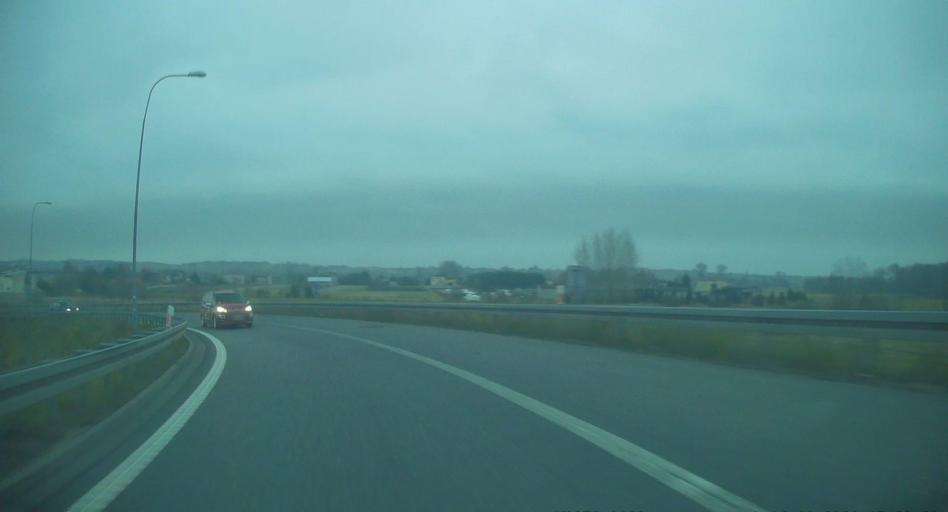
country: PL
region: Silesian Voivodeship
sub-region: Powiat tarnogorski
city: Ozarowice
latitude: 50.4531
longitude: 19.0544
